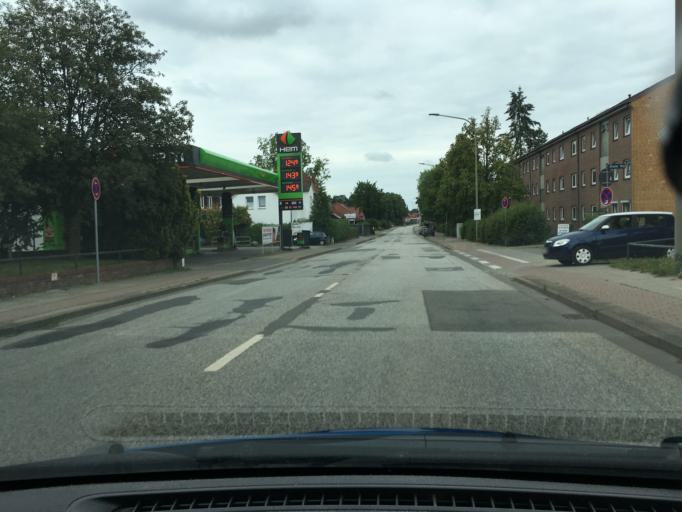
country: DE
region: Schleswig-Holstein
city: Geesthacht
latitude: 53.4491
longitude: 10.3599
